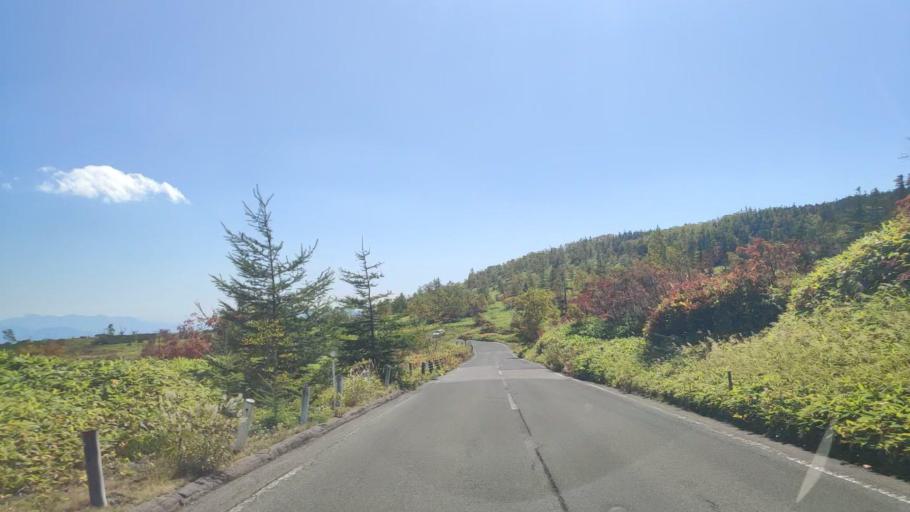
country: JP
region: Nagano
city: Nakano
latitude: 36.6358
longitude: 138.5402
